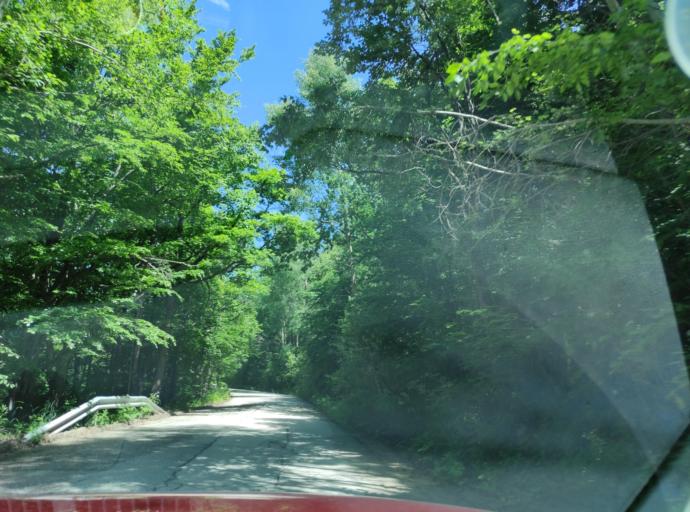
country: BG
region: Sofia-Capital
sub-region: Stolichna Obshtina
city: Sofia
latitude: 42.6313
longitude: 23.2320
